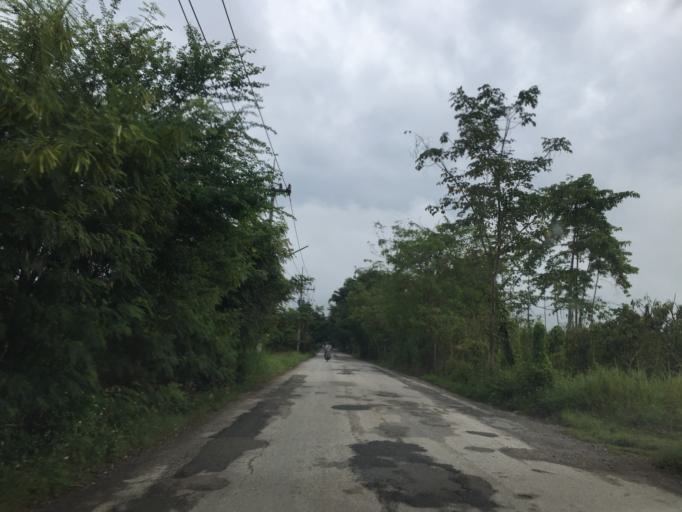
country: TH
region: Lamphun
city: Ban Thi
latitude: 18.6576
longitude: 99.0705
